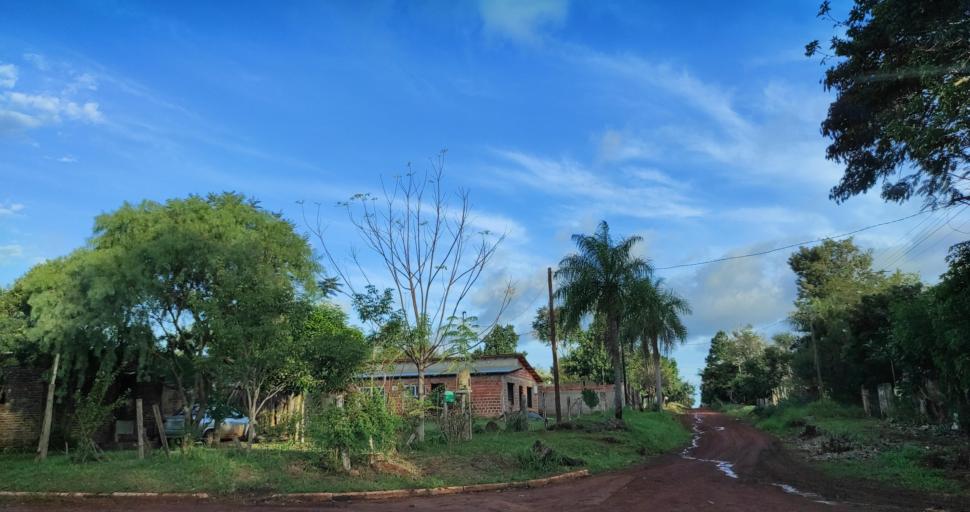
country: AR
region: Misiones
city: Garupa
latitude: -27.5217
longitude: -55.8566
